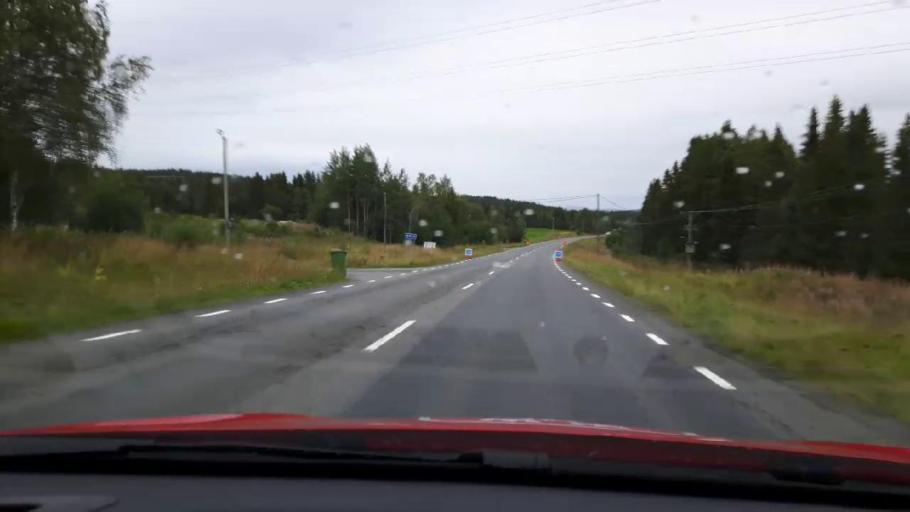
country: SE
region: Jaemtland
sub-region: Are Kommun
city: Jarpen
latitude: 63.3807
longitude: 13.4243
